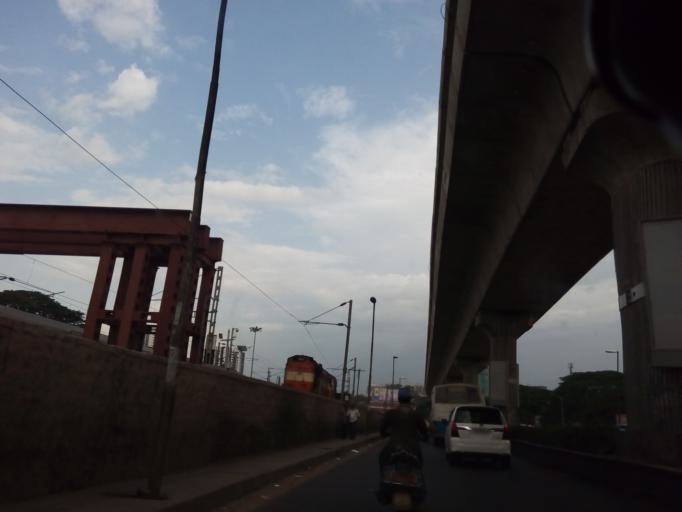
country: IN
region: Karnataka
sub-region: Bangalore Urban
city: Bangalore
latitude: 13.0214
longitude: 77.5521
